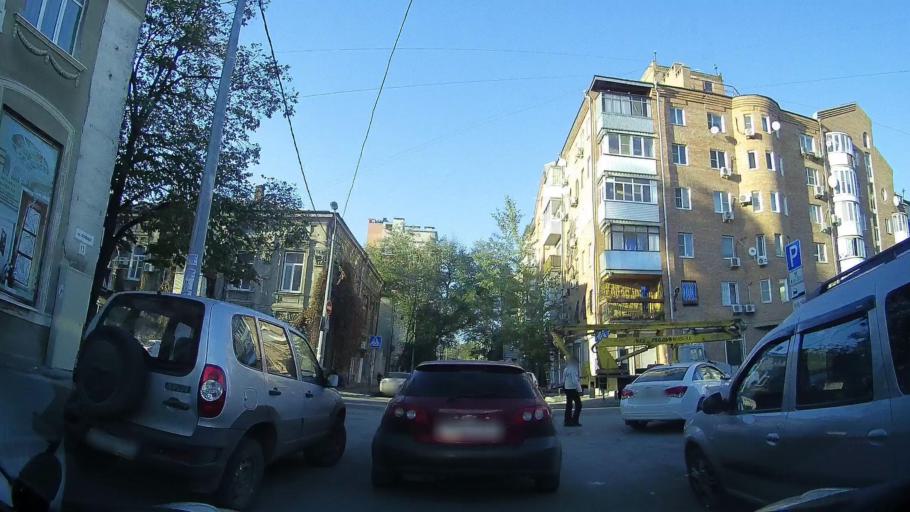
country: RU
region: Rostov
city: Rostov-na-Donu
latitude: 47.2152
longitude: 39.7070
